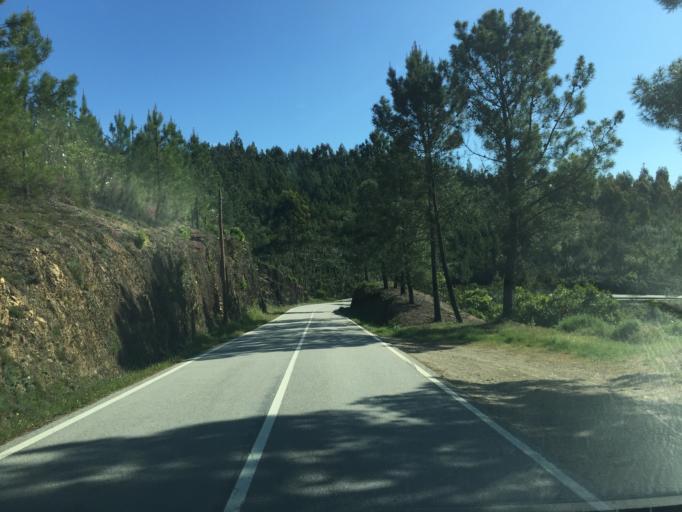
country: PT
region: Coimbra
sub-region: Pampilhosa da Serra
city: Pampilhosa da Serra
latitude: 40.0436
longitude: -7.8782
